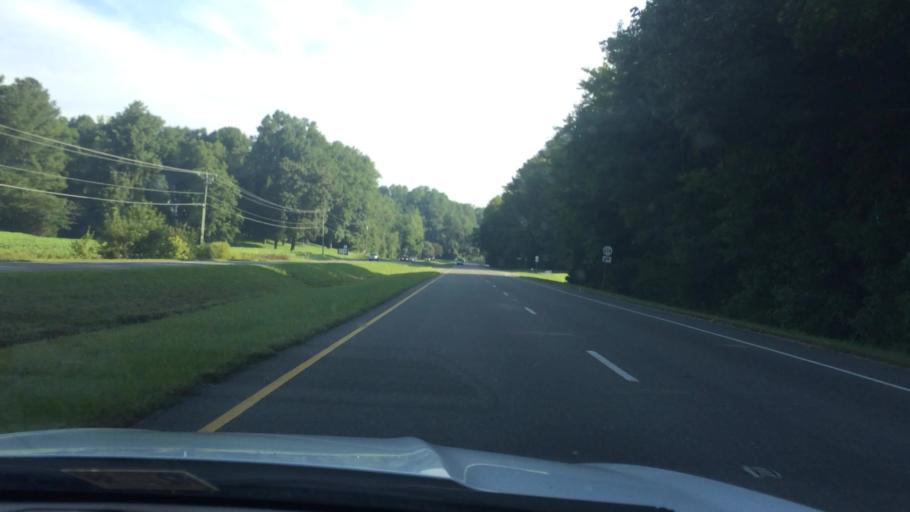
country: US
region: Virginia
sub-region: Gloucester County
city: Gloucester Courthouse
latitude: 37.4481
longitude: -76.4727
